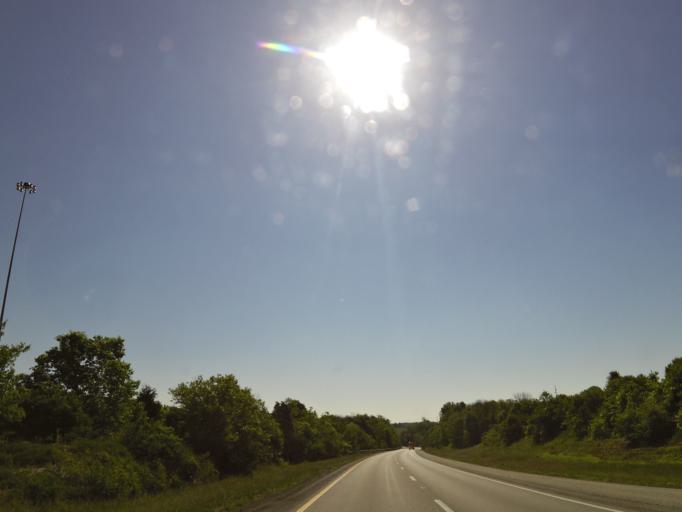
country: US
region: Kentucky
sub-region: Franklin County
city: Frankfort
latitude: 38.1582
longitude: -84.8918
